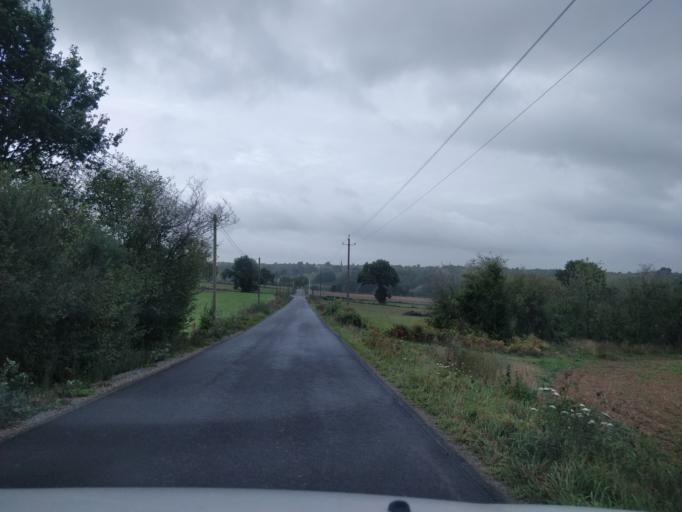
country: FR
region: Brittany
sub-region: Departement d'Ille-et-Vilaine
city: La Bouexiere
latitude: 48.1998
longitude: -1.4355
